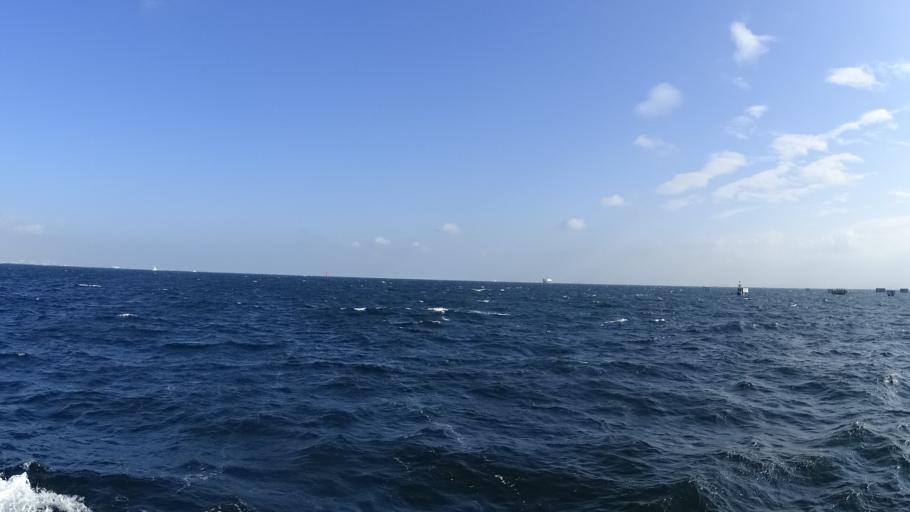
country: JP
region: Kanagawa
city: Yokosuka
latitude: 35.3045
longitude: 139.6588
